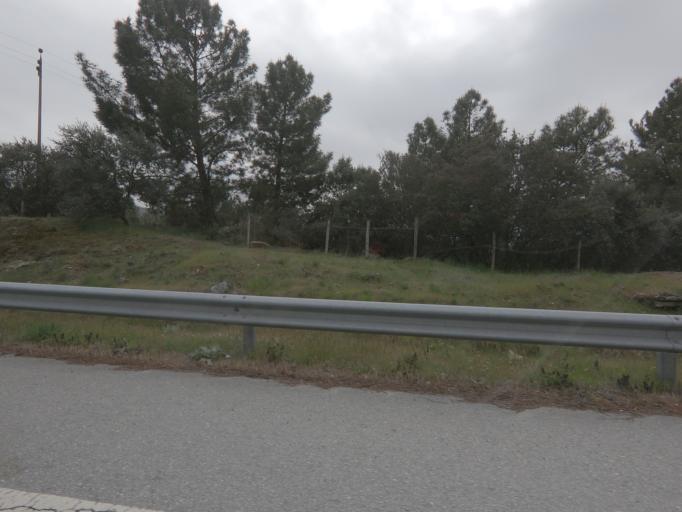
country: PT
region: Guarda
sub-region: Celorico da Beira
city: Celorico da Beira
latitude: 40.6391
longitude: -7.3250
